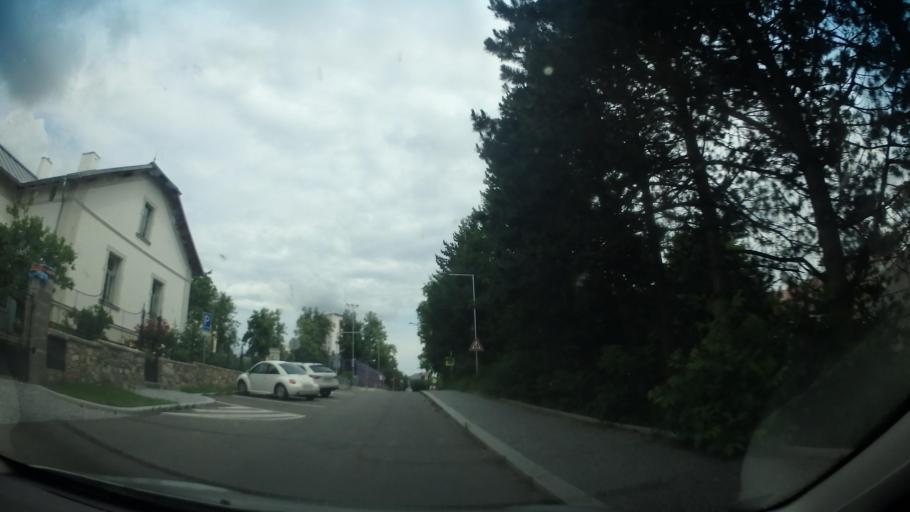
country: CZ
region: Vysocina
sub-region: Okres Zd'ar nad Sazavou
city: Nove Mesto na Morave
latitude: 49.5627
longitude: 16.0728
